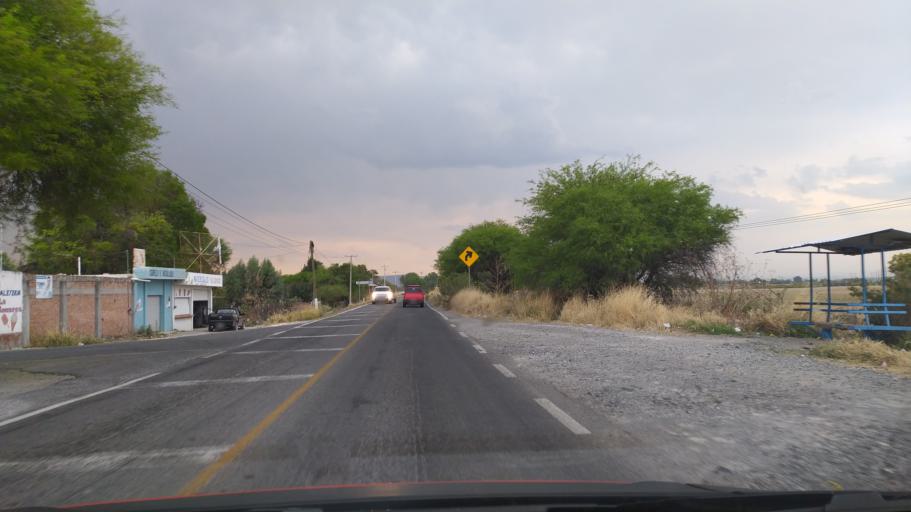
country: MX
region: Guanajuato
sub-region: San Francisco del Rincon
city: San Ignacio de Hidalgo
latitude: 20.8285
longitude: -101.9005
